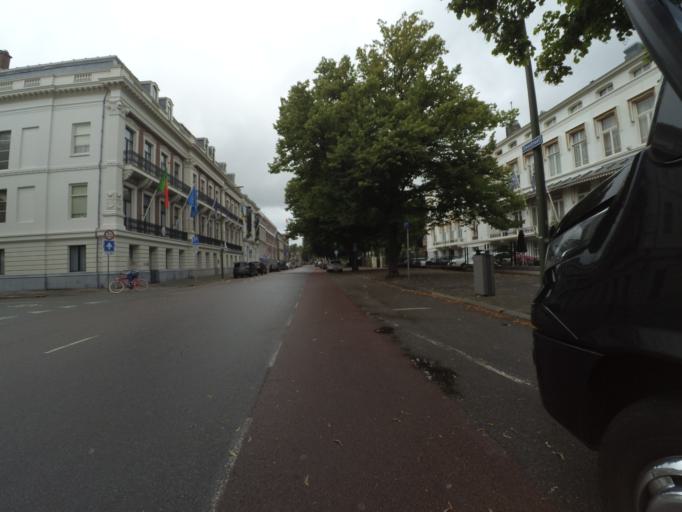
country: NL
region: South Holland
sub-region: Gemeente Den Haag
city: The Hague
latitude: 52.0856
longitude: 4.3023
